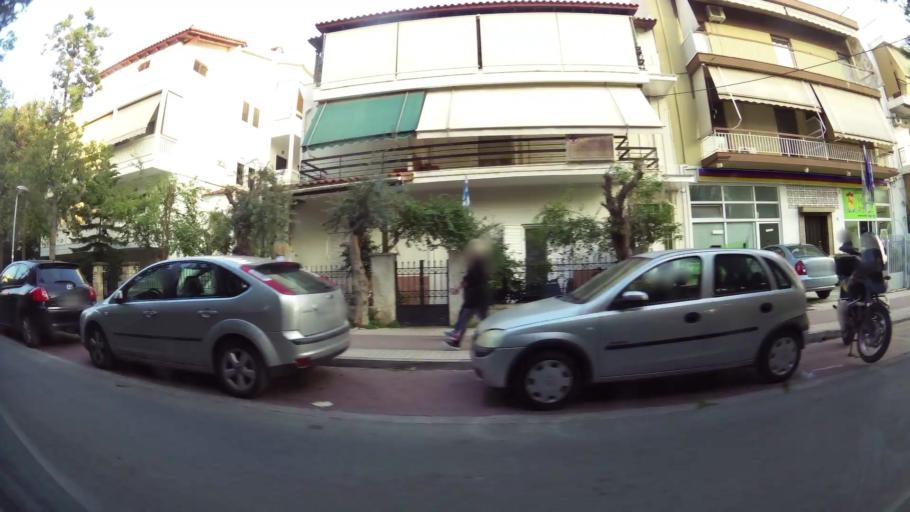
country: GR
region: Attica
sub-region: Nomarchia Athinas
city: Agia Paraskevi
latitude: 38.0201
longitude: 23.8303
